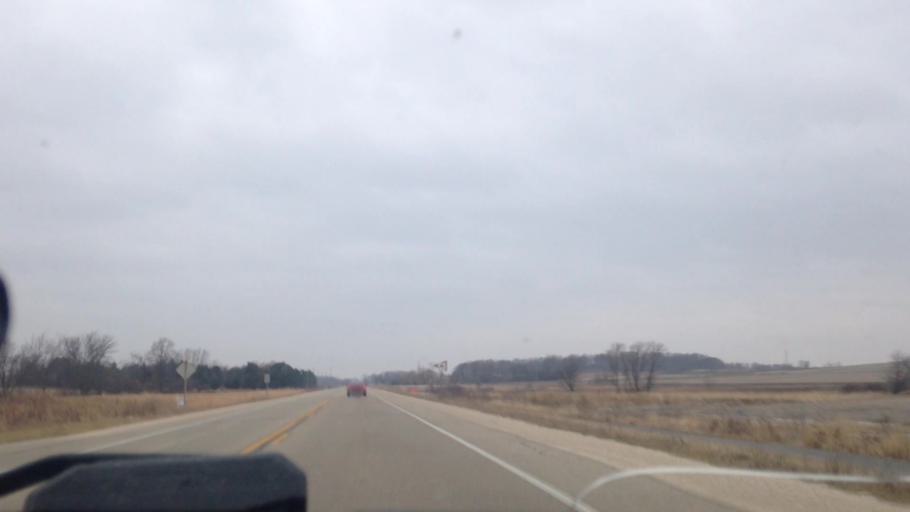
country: US
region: Wisconsin
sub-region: Dodge County
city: Mayville
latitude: 43.4909
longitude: -88.5732
